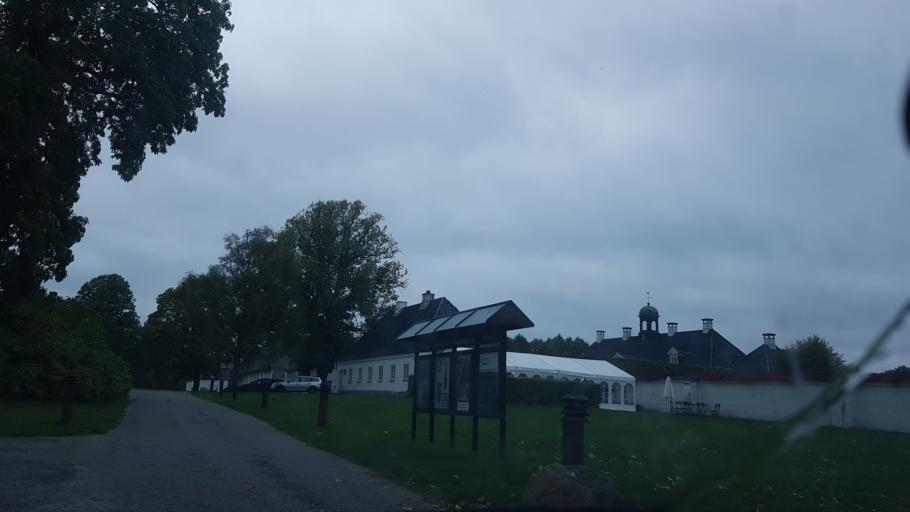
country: DK
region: Capital Region
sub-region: Rudersdal Kommune
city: Trorod
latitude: 55.8281
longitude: 12.5167
